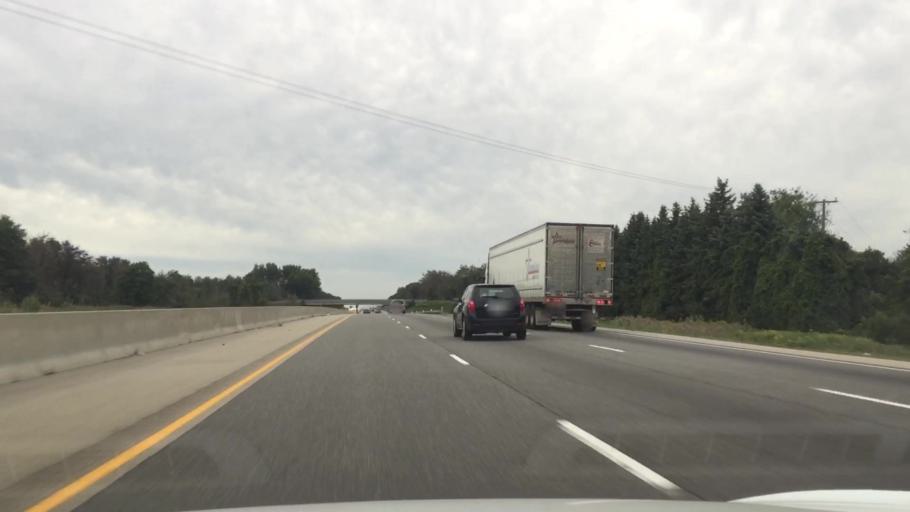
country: CA
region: Ontario
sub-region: Oxford County
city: Woodstock
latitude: 43.1693
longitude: -80.6607
